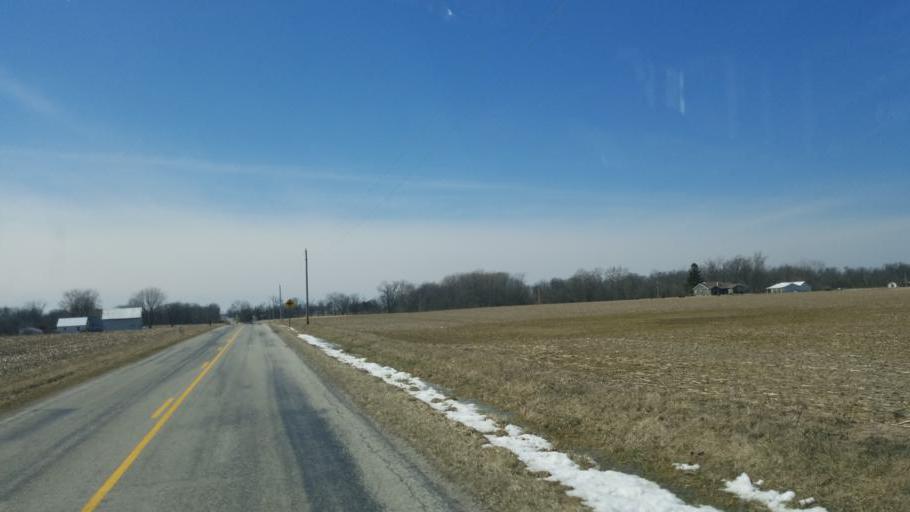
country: US
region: Ohio
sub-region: Crawford County
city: Bucyrus
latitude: 40.6750
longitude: -82.9348
